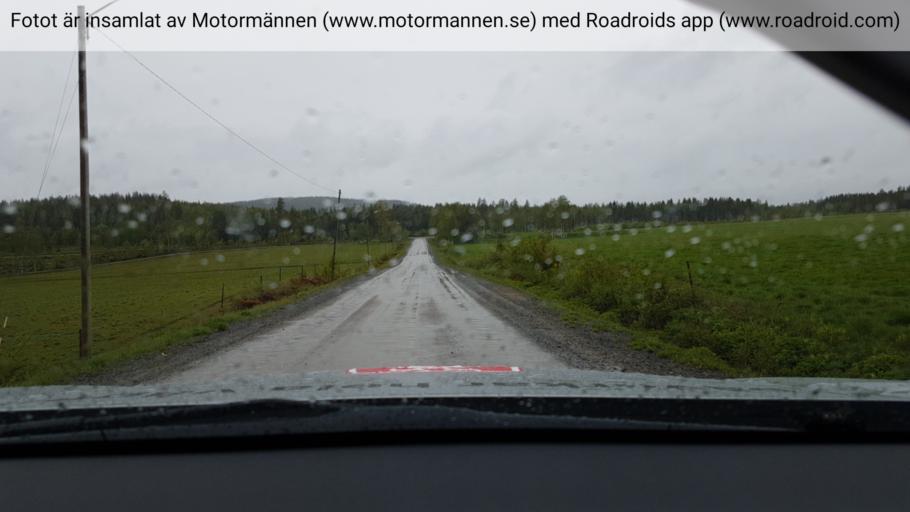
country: SE
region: Vaesterbotten
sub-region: Vannas Kommun
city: Vaennaes
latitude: 63.8557
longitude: 19.6300
